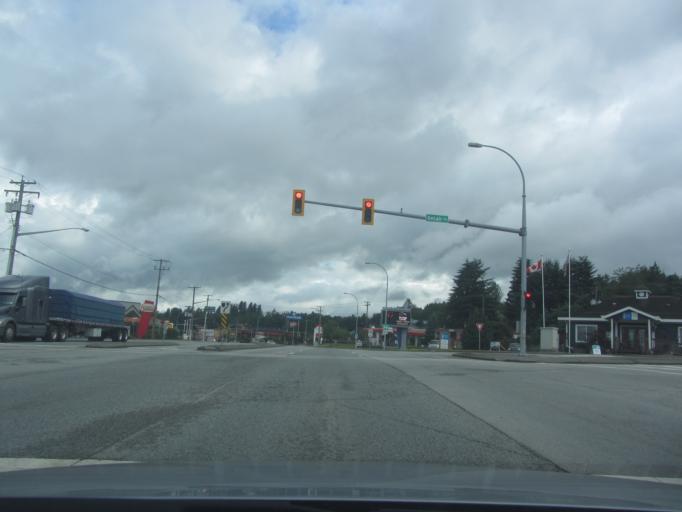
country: CA
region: British Columbia
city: Abbotsford
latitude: 49.0363
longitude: -122.2675
